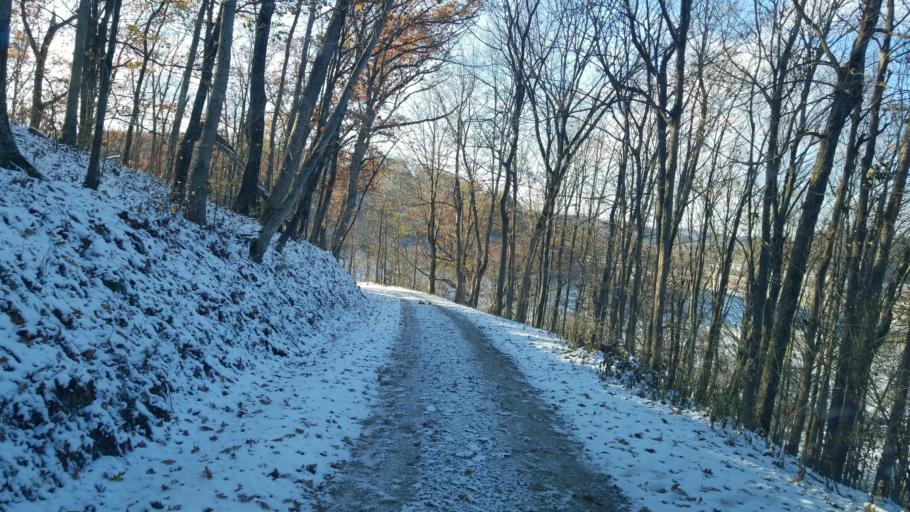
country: US
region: Ohio
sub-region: Licking County
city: Utica
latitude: 40.1629
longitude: -82.3960
